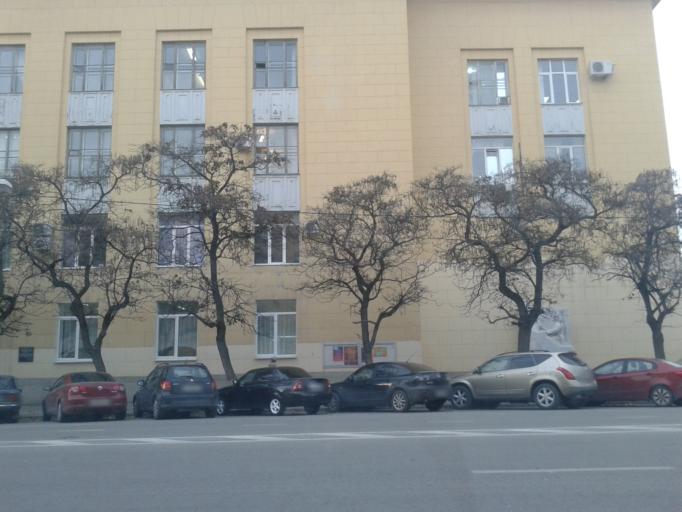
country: RU
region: Volgograd
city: Volgograd
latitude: 48.7070
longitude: 44.5120
